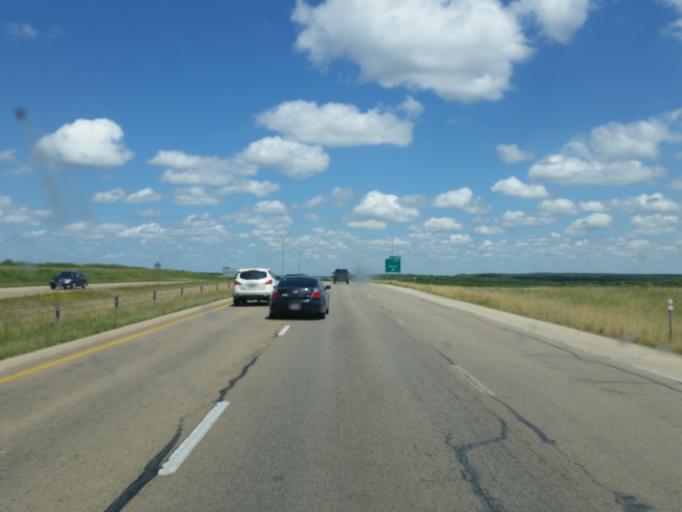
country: US
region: Texas
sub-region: Callahan County
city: Baird
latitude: 32.4000
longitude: -99.3796
